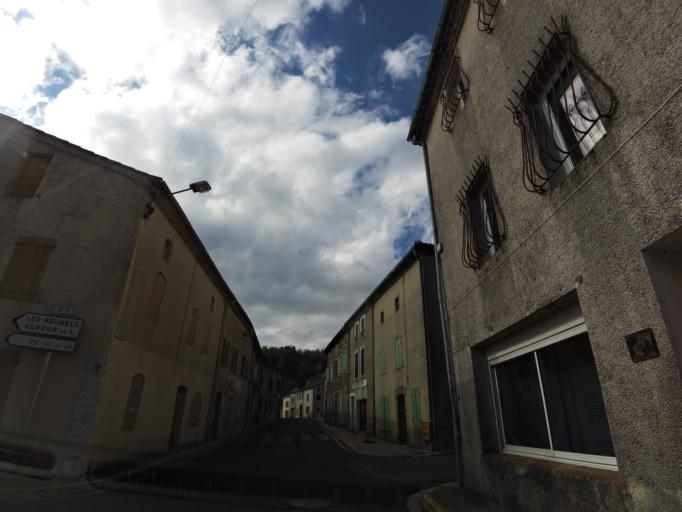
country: FR
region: Midi-Pyrenees
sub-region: Departement du Tarn
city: Soreze
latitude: 43.4116
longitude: 2.0789
